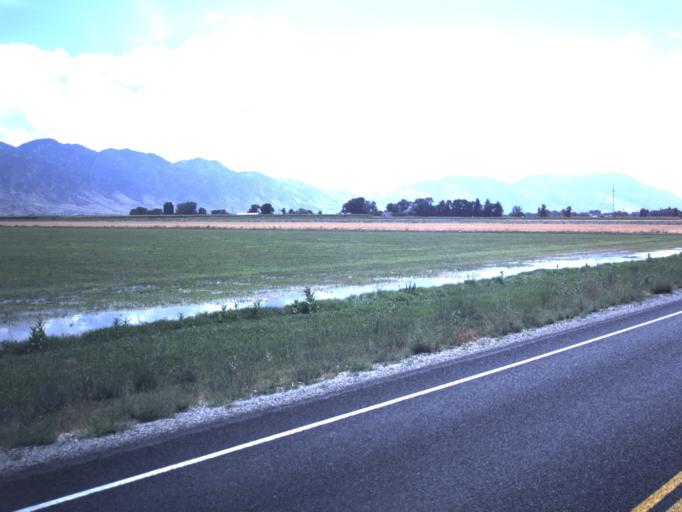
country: US
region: Utah
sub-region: Box Elder County
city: Elwood
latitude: 41.6542
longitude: -112.1403
